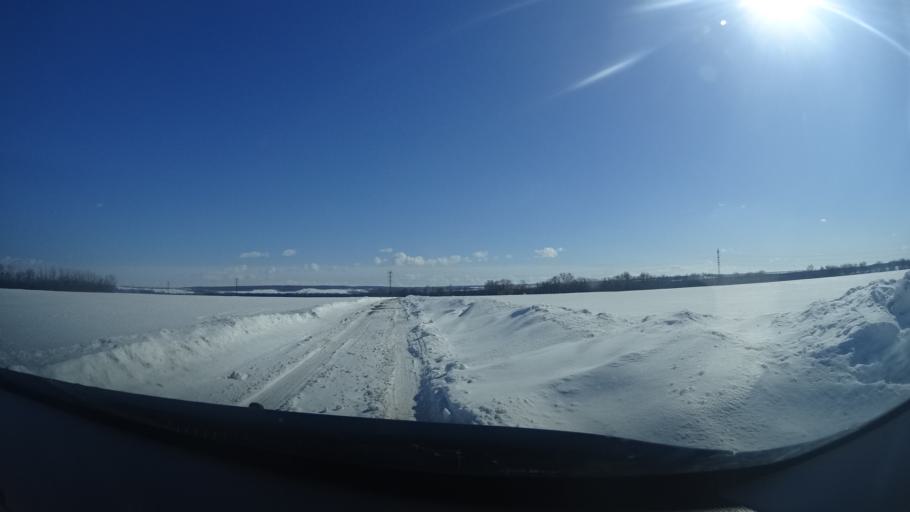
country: RU
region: Bashkortostan
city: Chishmy
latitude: 54.5874
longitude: 55.4090
